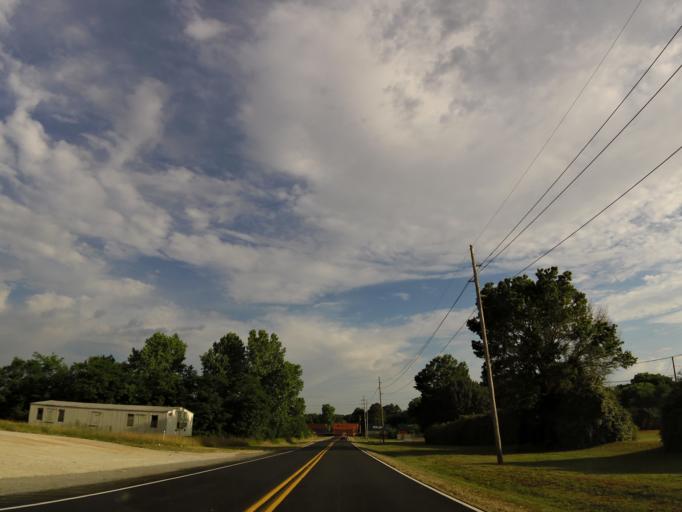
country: US
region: Alabama
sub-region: Morgan County
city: Trinity
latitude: 34.6082
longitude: -87.0512
